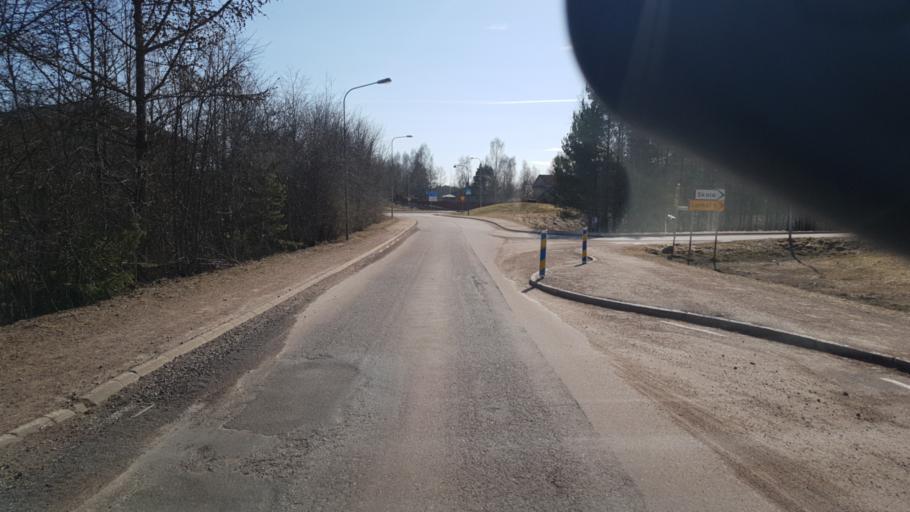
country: SE
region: Vaermland
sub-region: Arvika Kommun
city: Arvika
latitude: 59.6313
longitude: 12.8191
